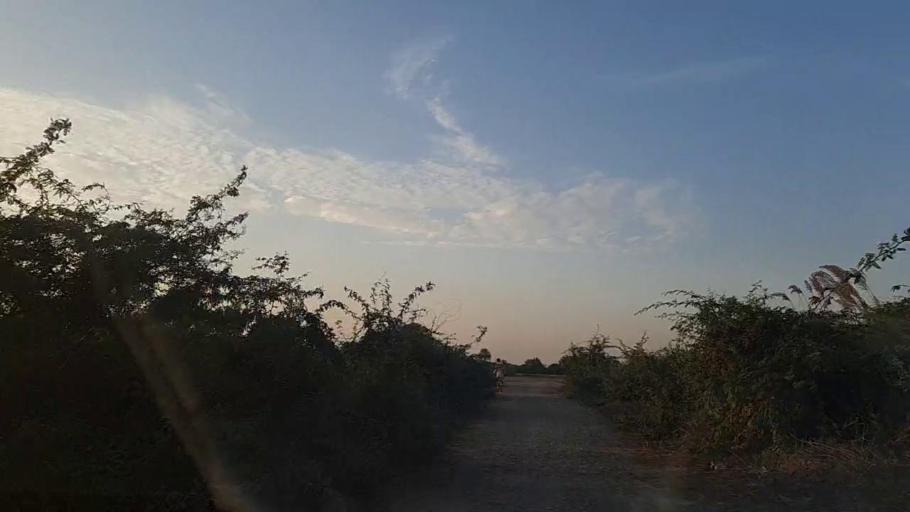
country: PK
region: Sindh
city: Chuhar Jamali
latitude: 24.4492
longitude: 68.1175
